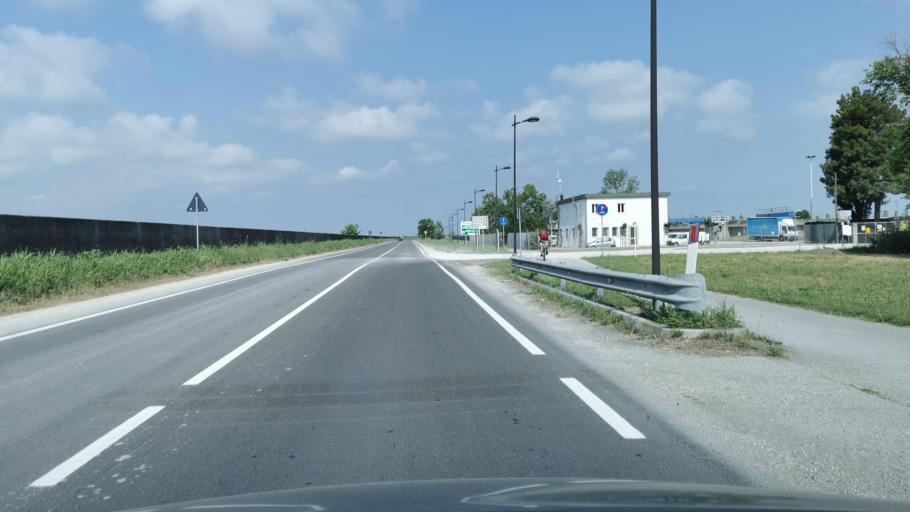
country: IT
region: Emilia-Romagna
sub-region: Provincia di Ferrara
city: Porto Garibaldi
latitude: 44.6773
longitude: 12.2106
